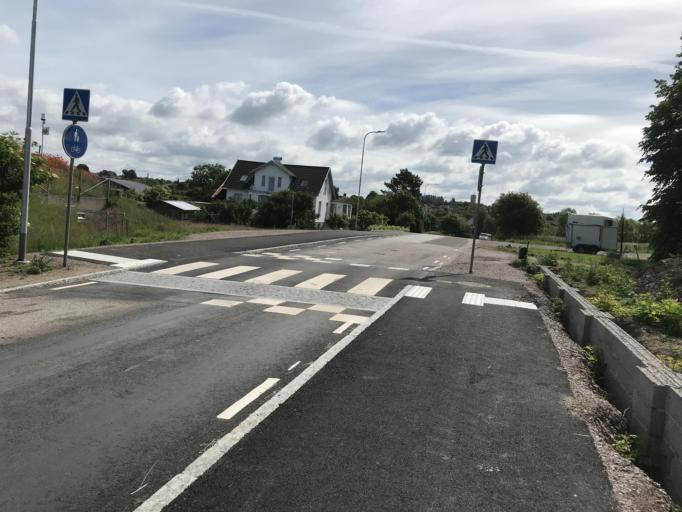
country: SE
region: Skane
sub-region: Helsingborg
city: Glumslov
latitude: 55.9408
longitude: 12.8004
